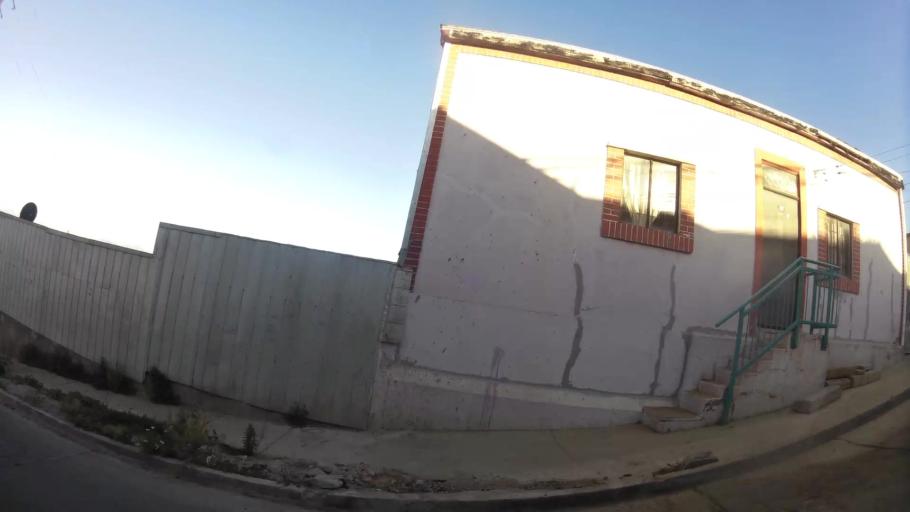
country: CL
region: Valparaiso
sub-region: Provincia de Valparaiso
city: Valparaiso
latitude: -33.0573
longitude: -71.6128
